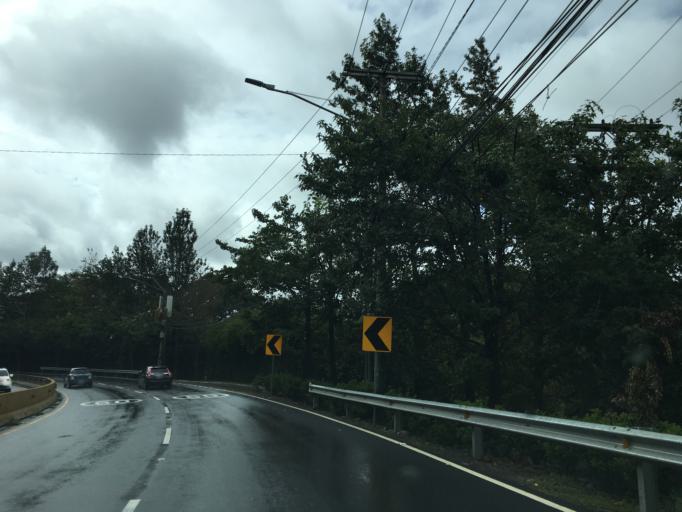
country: GT
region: Guatemala
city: Santa Catarina Pinula
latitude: 14.5793
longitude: -90.4877
